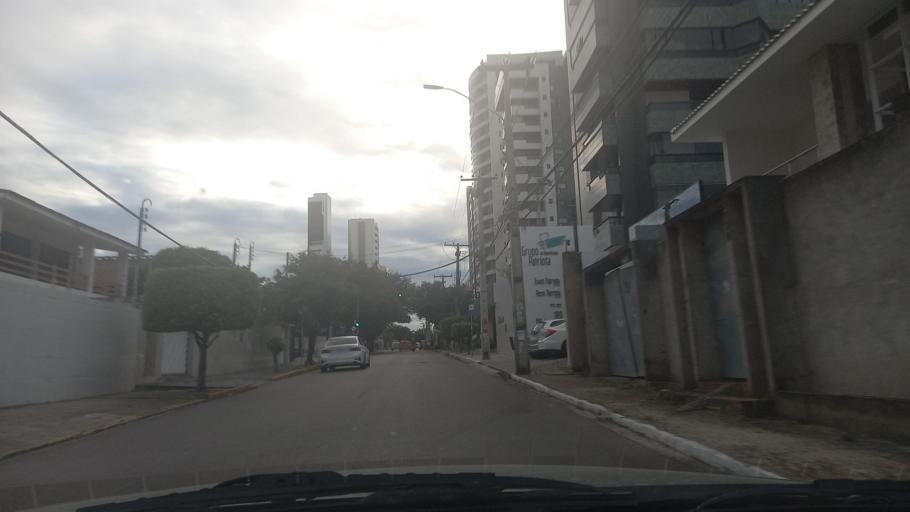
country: BR
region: Pernambuco
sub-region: Caruaru
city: Caruaru
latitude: -8.2700
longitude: -35.9709
